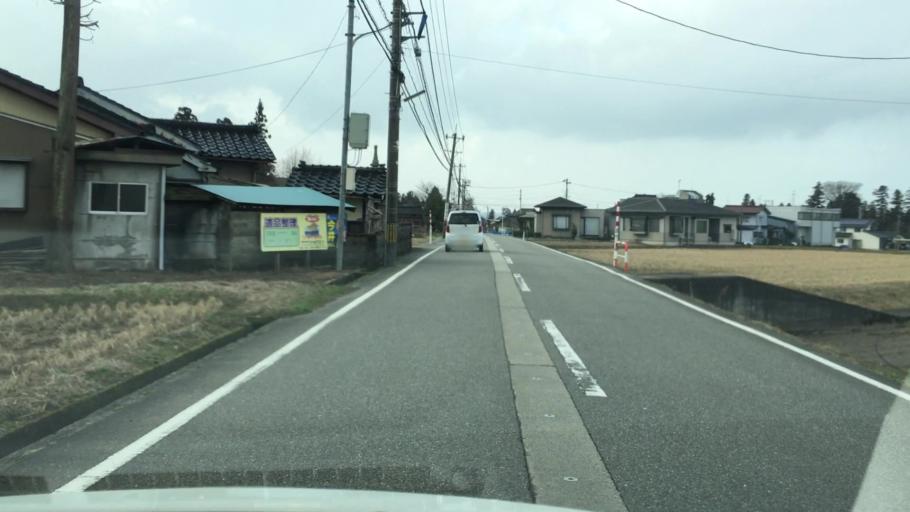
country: JP
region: Toyama
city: Toyama-shi
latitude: 36.6607
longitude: 137.2711
